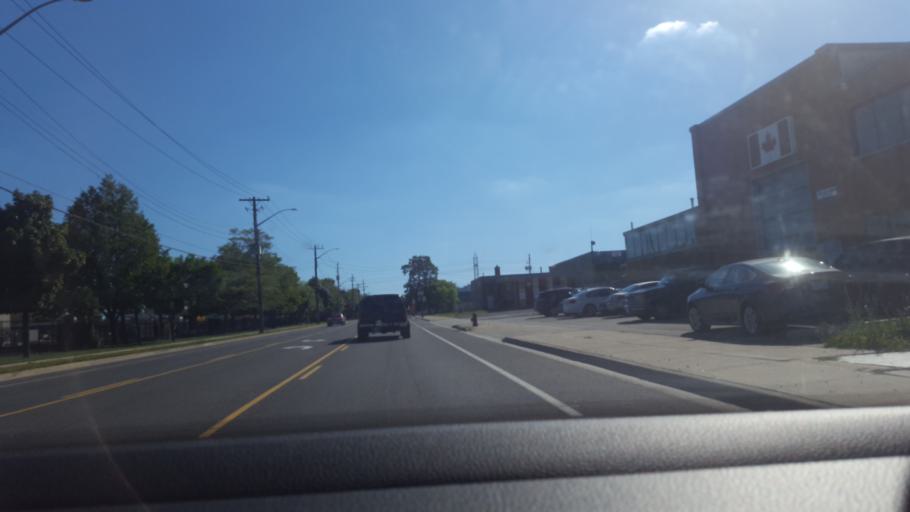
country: CA
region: Ontario
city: Hamilton
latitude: 43.2527
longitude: -79.7746
